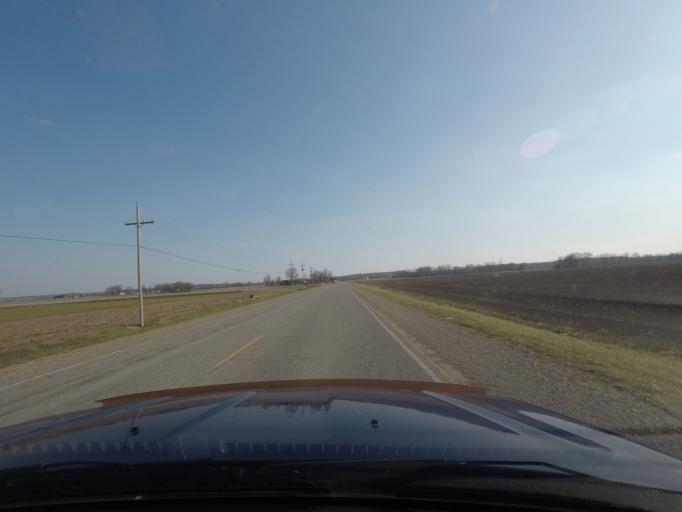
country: US
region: Kansas
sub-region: Jefferson County
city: Oskaloosa
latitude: 39.0681
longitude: -95.3820
